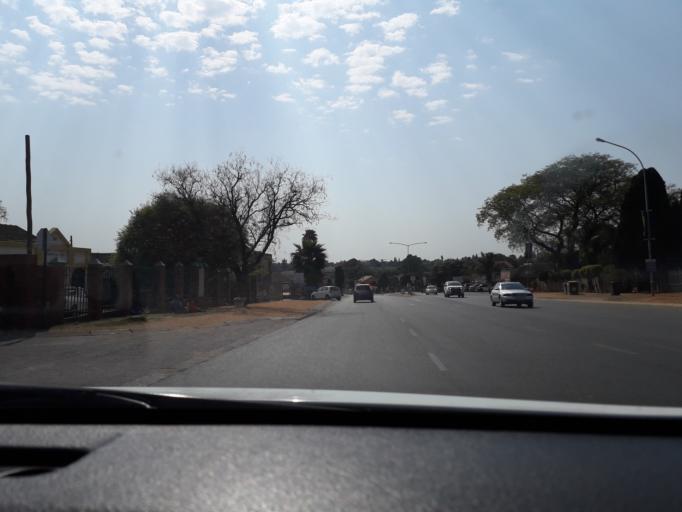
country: ZA
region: Gauteng
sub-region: Ekurhuleni Metropolitan Municipality
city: Tembisa
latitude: -26.0785
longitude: 28.2501
